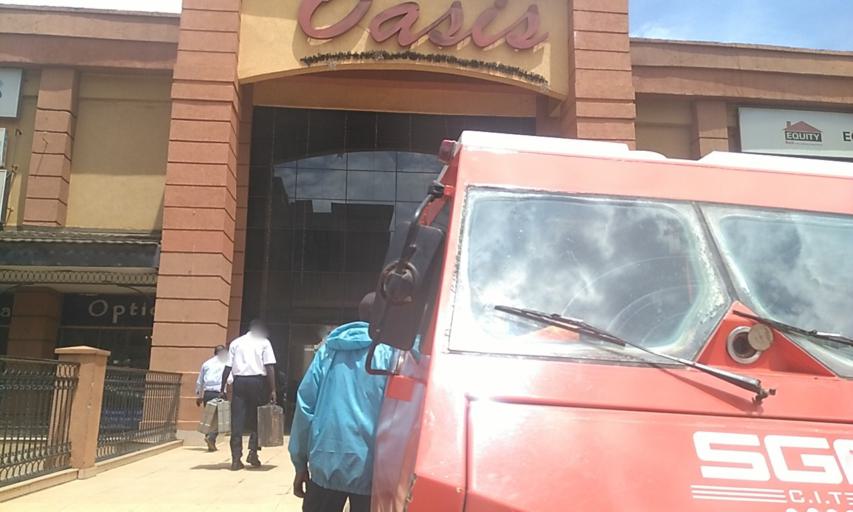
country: UG
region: Central Region
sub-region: Kampala District
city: Kampala
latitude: 0.3188
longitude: 32.5924
